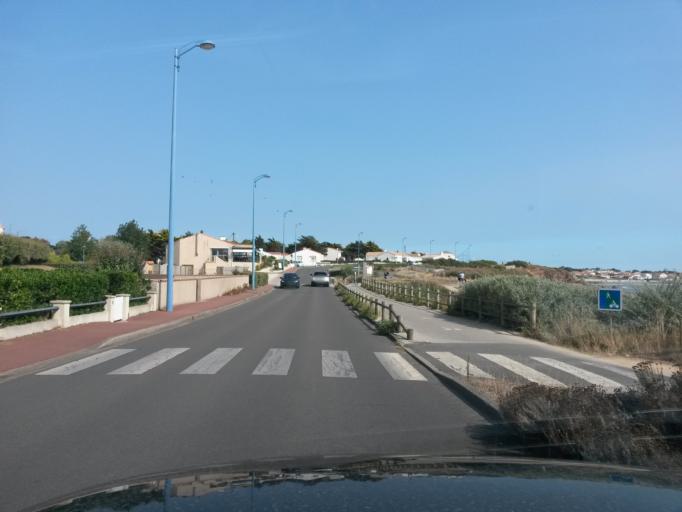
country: FR
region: Pays de la Loire
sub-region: Departement de la Vendee
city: Bretignolles-sur-Mer
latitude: 46.6317
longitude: -1.8830
